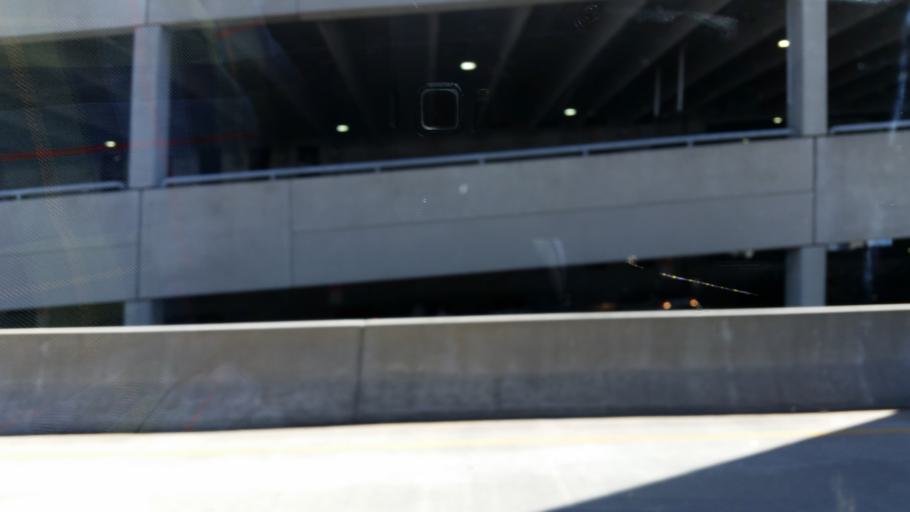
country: US
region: Georgia
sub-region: Fulton County
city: Hapeville
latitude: 33.6415
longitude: -84.4186
